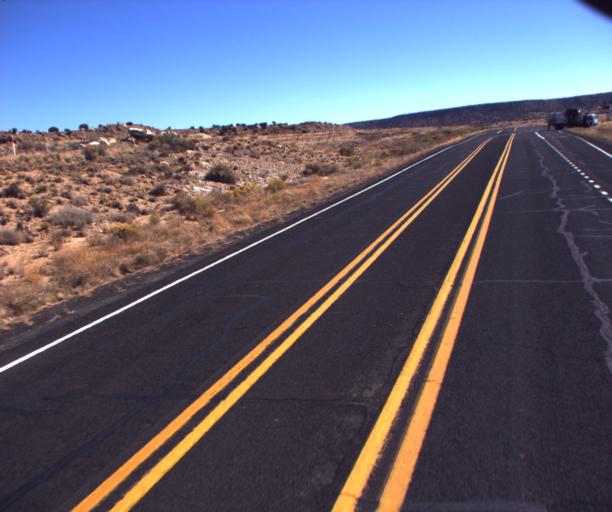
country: US
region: Arizona
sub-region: Navajo County
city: First Mesa
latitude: 35.8338
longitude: -110.2967
